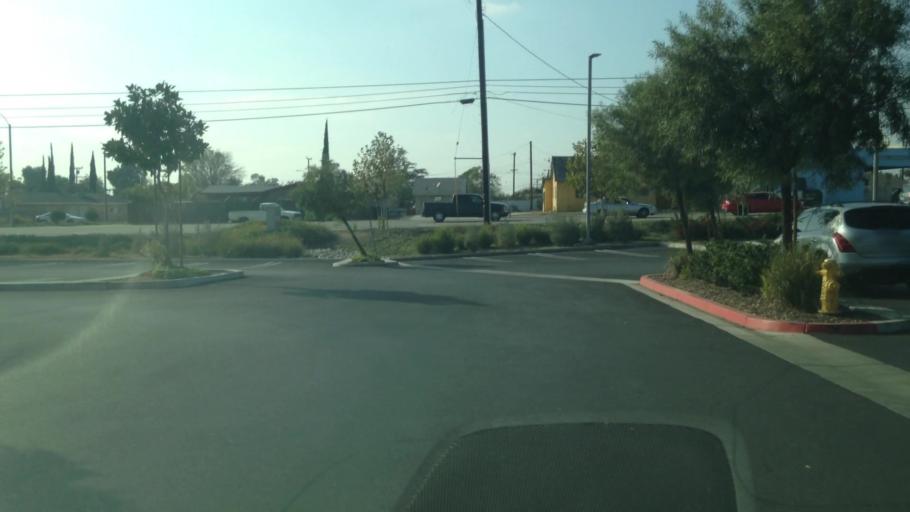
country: US
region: California
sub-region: San Bernardino County
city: Fontana
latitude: 34.0697
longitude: -117.4436
